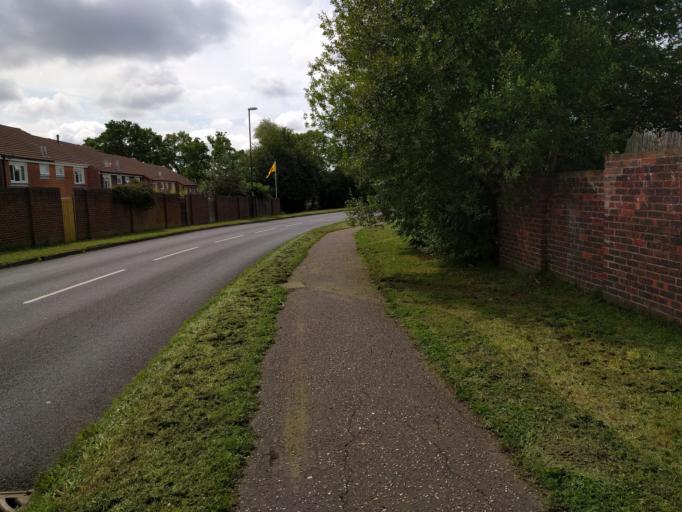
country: GB
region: England
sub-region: West Sussex
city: Bewbush
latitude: 51.1101
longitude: -0.2301
